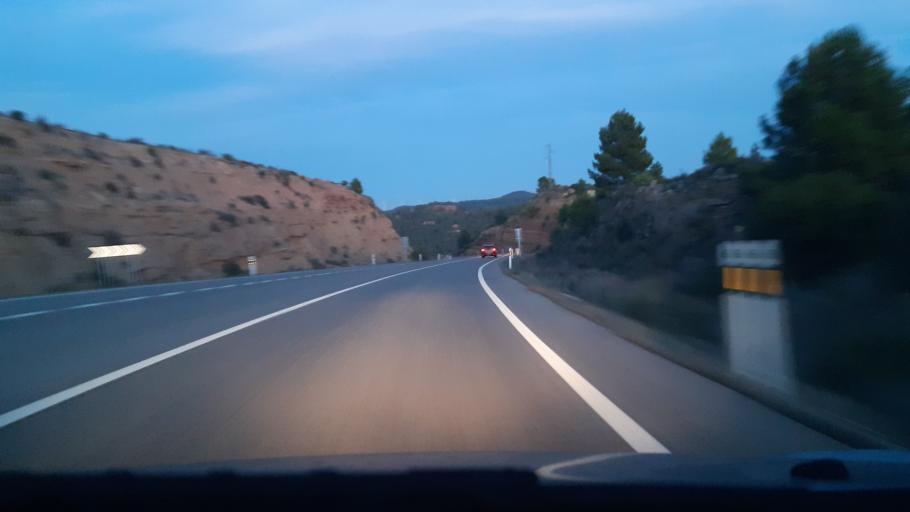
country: ES
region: Aragon
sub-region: Provincia de Teruel
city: Calaceite
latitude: 41.0224
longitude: 0.2173
